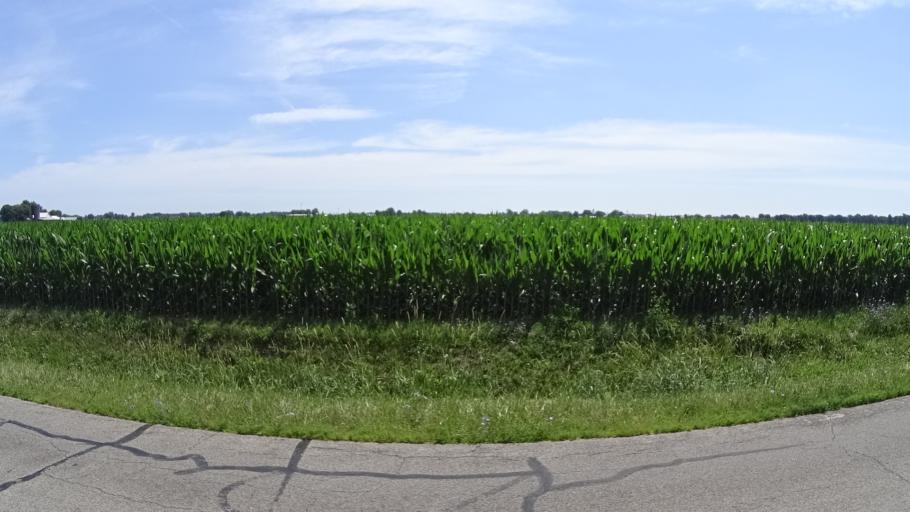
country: US
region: Ohio
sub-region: Erie County
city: Sandusky
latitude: 41.4159
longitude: -82.7887
